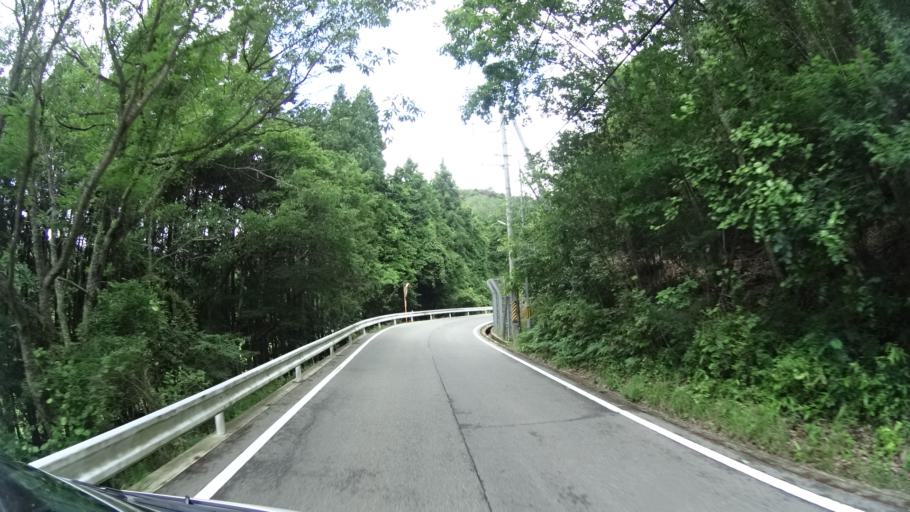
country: JP
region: Hyogo
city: Sasayama
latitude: 35.0232
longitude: 135.3923
